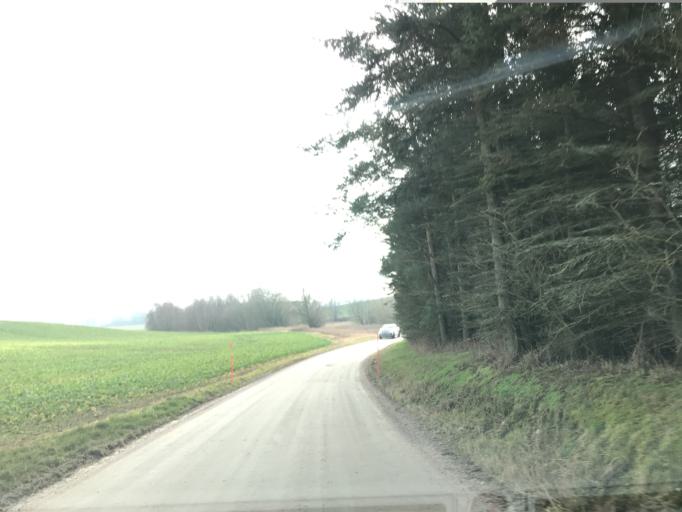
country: SE
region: Skane
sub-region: Svalovs Kommun
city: Teckomatorp
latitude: 55.8334
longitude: 13.0721
